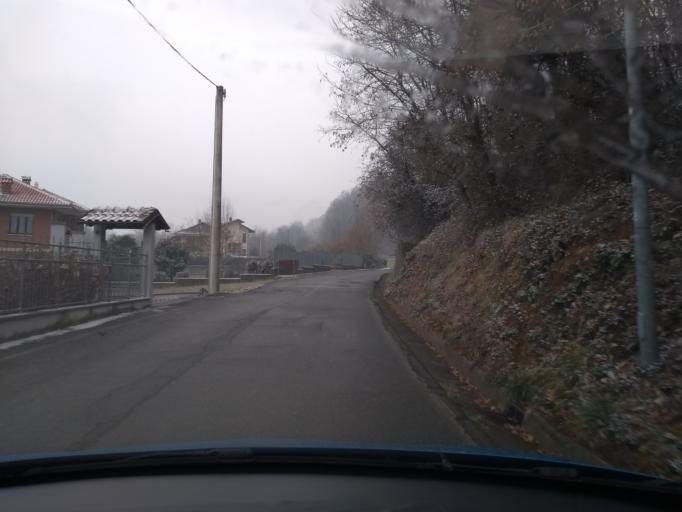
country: IT
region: Piedmont
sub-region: Provincia di Torino
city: Balangero
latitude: 45.2772
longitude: 7.5142
